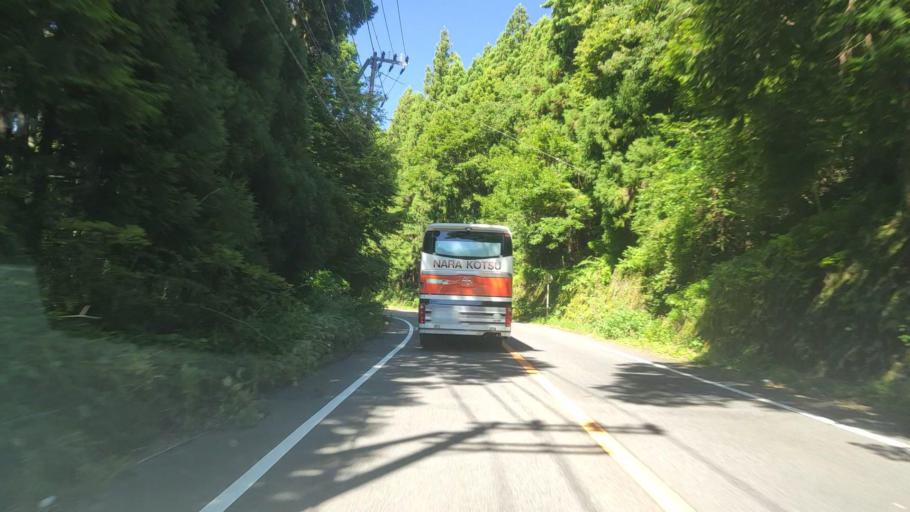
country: JP
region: Nara
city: Haibara-akanedai
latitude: 34.5273
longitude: 135.9416
